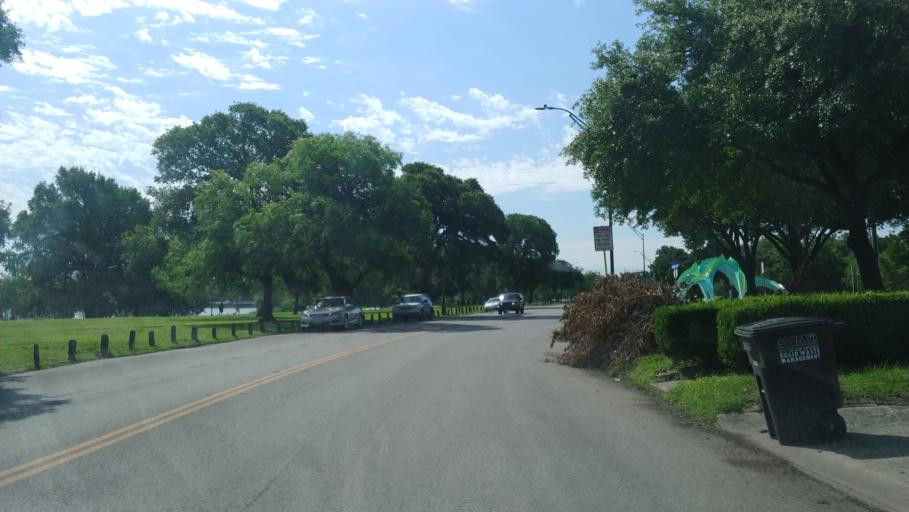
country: US
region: Texas
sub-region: Bexar County
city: Balcones Heights
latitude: 29.4515
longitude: -98.5356
